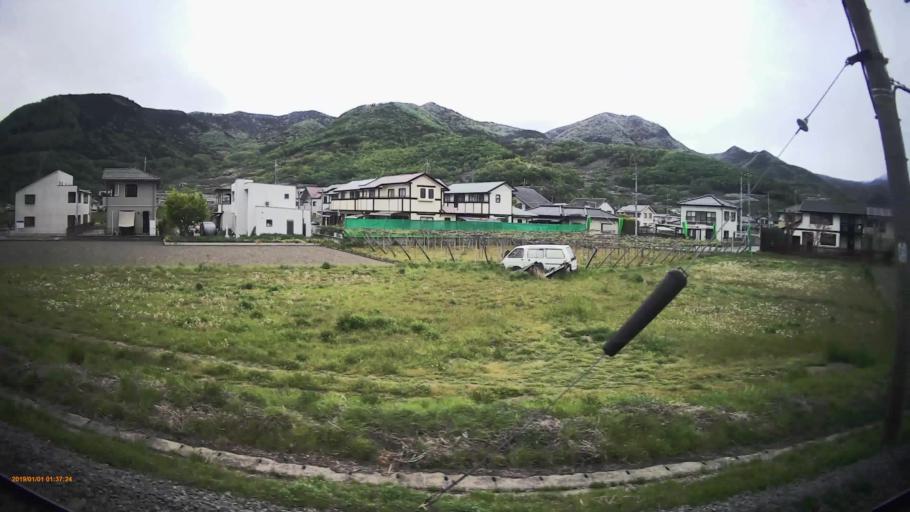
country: JP
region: Yamanashi
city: Isawa
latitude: 35.6666
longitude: 138.6502
